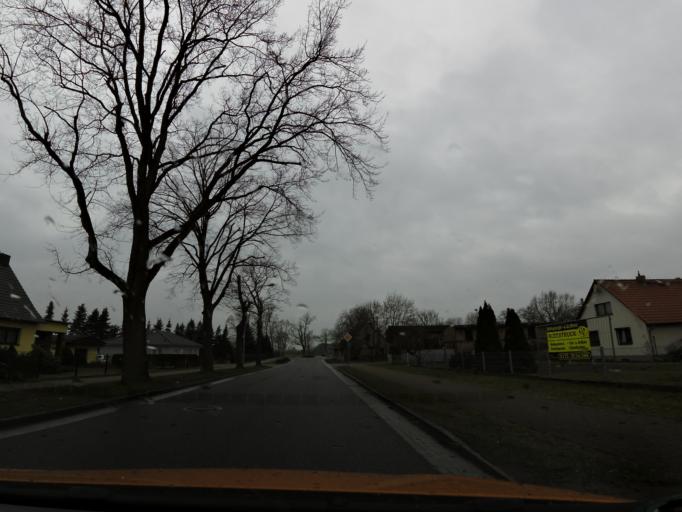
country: DE
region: Brandenburg
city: Roskow
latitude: 52.4096
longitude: 12.6896
